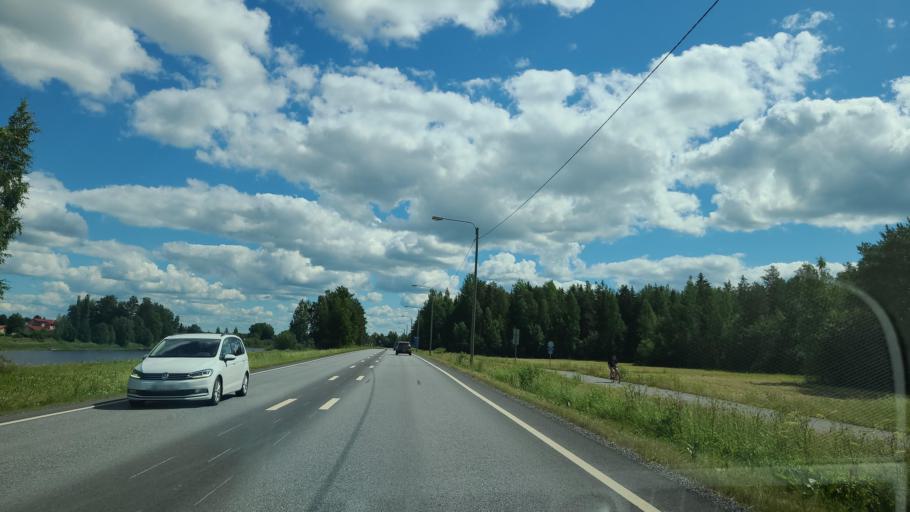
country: FI
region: Ostrobothnia
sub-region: Kyroenmaa
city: Isokyroe
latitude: 62.9746
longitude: 22.3697
